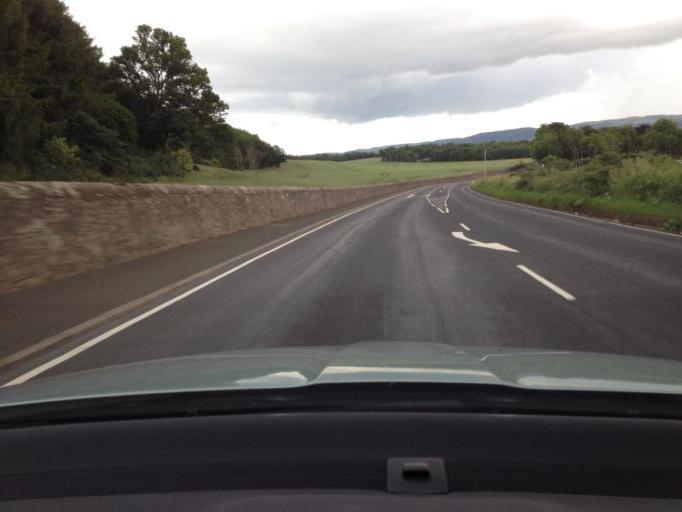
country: GB
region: Scotland
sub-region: Perth and Kinross
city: Bridge of Earn
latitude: 56.3640
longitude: -3.4248
